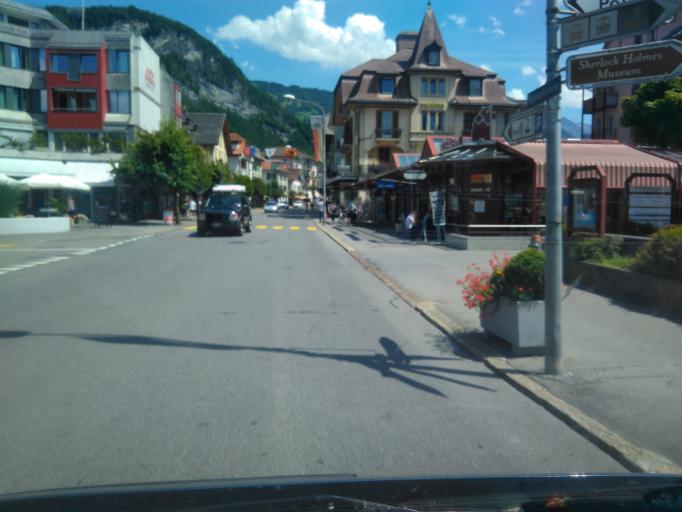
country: CH
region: Bern
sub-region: Interlaken-Oberhasli District
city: Meiringen
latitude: 46.7281
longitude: 8.1849
